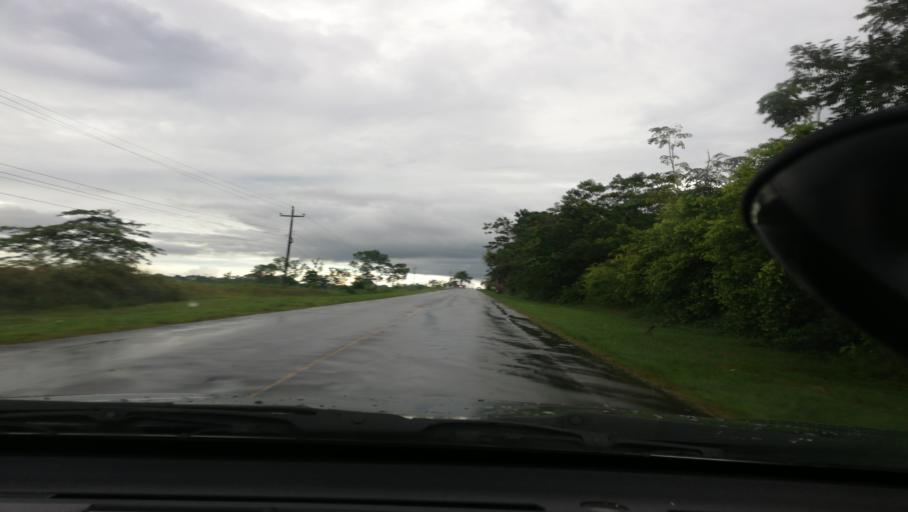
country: PE
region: Loreto
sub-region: Provincia de Maynas
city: Iquitos
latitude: -3.8969
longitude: -73.3486
